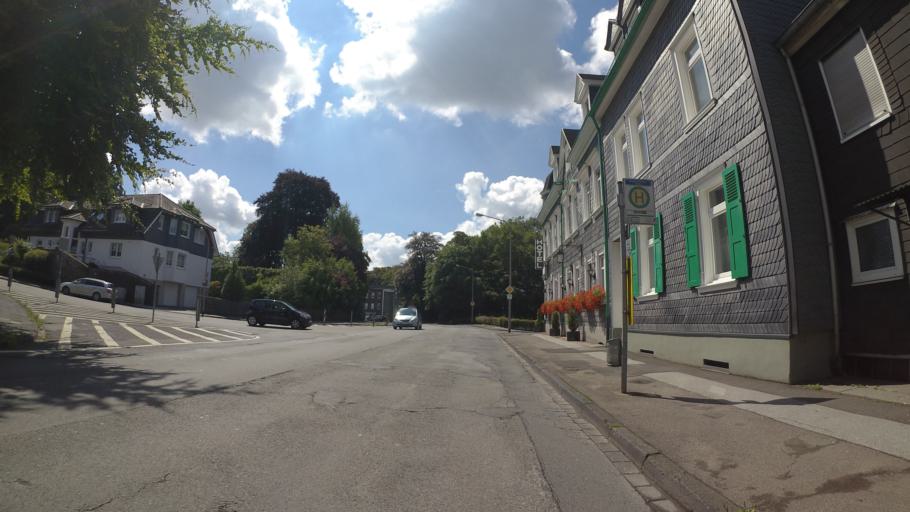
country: DE
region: North Rhine-Westphalia
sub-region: Regierungsbezirk Dusseldorf
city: Remscheid
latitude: 51.1957
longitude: 7.2518
